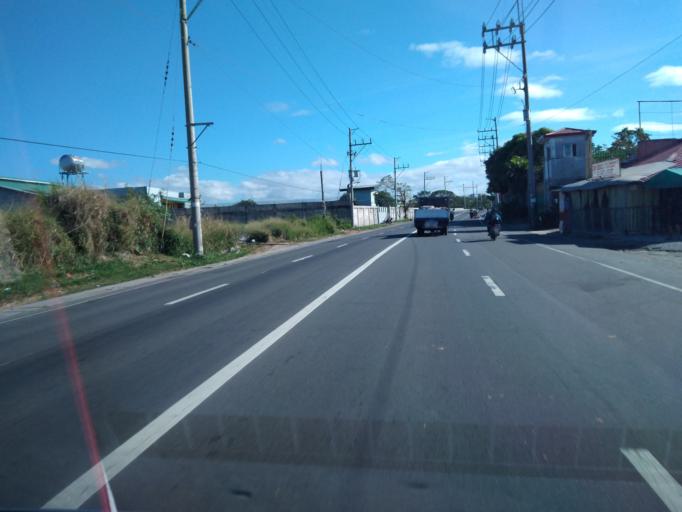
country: PH
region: Central Luzon
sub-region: Province of Bulacan
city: Santa Maria
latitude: 14.8270
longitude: 120.9572
